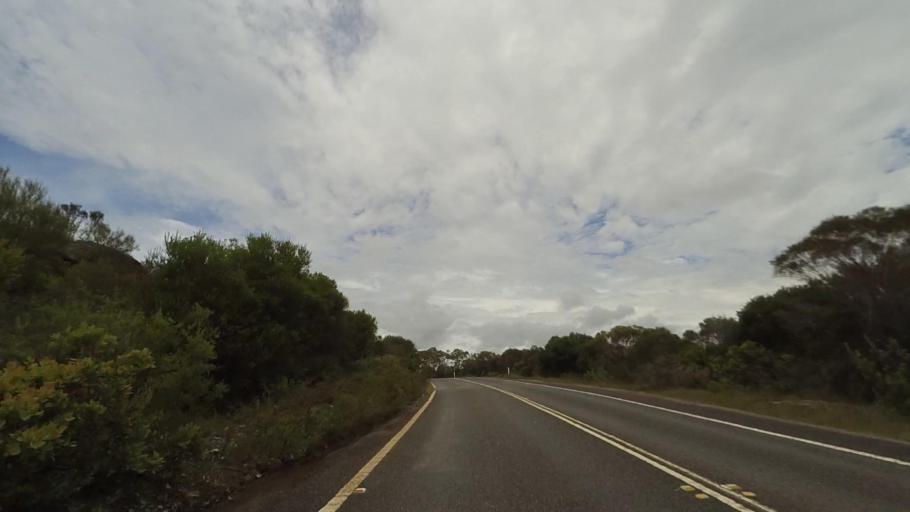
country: AU
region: New South Wales
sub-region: Sutherland Shire
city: Grays Point
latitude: -34.1232
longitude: 151.0791
